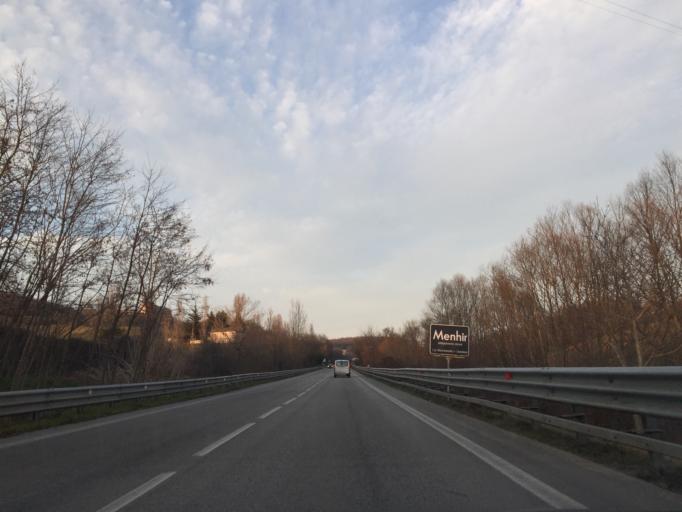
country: IT
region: Molise
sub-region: Provincia di Campobasso
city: Mimosa-Poggio Verde-Nuova Comunita
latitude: 41.5391
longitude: 14.6181
